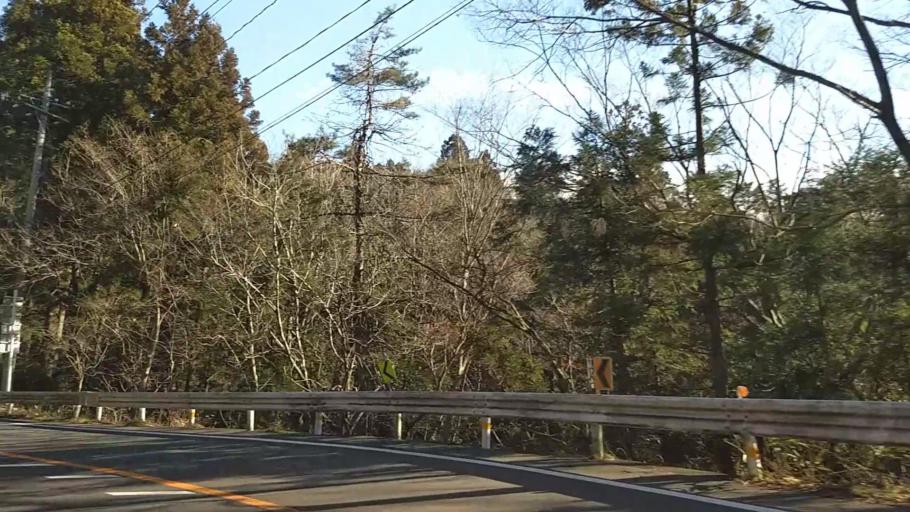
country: JP
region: Yamanashi
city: Uenohara
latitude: 35.5318
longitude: 139.0943
